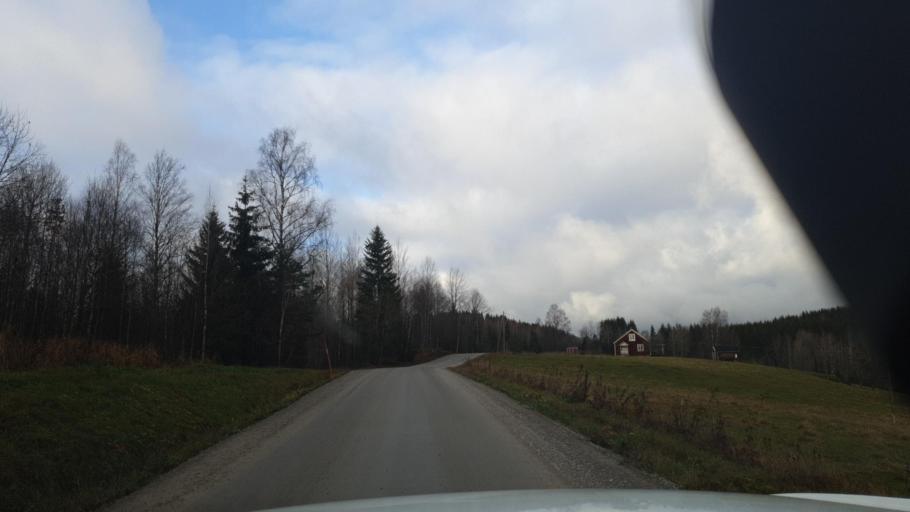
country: SE
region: Vaermland
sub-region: Sunne Kommun
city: Sunne
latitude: 59.6819
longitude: 12.8958
